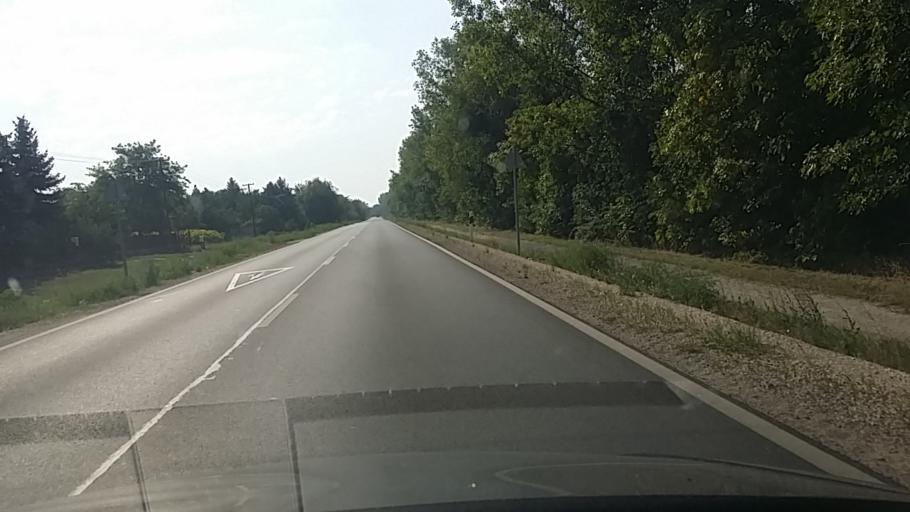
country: HU
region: Bekes
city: Szarvas
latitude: 46.8277
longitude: 20.6531
